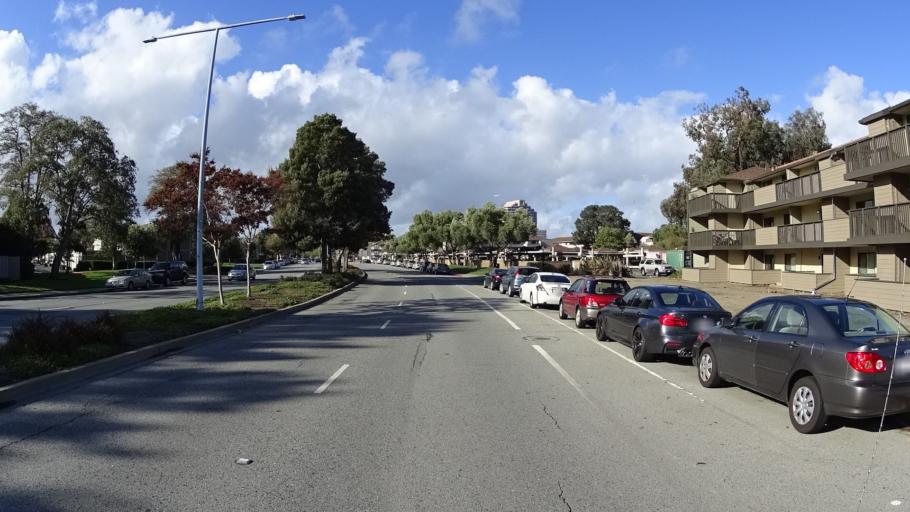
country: US
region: California
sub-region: San Mateo County
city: Foster City
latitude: 37.5510
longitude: -122.2745
